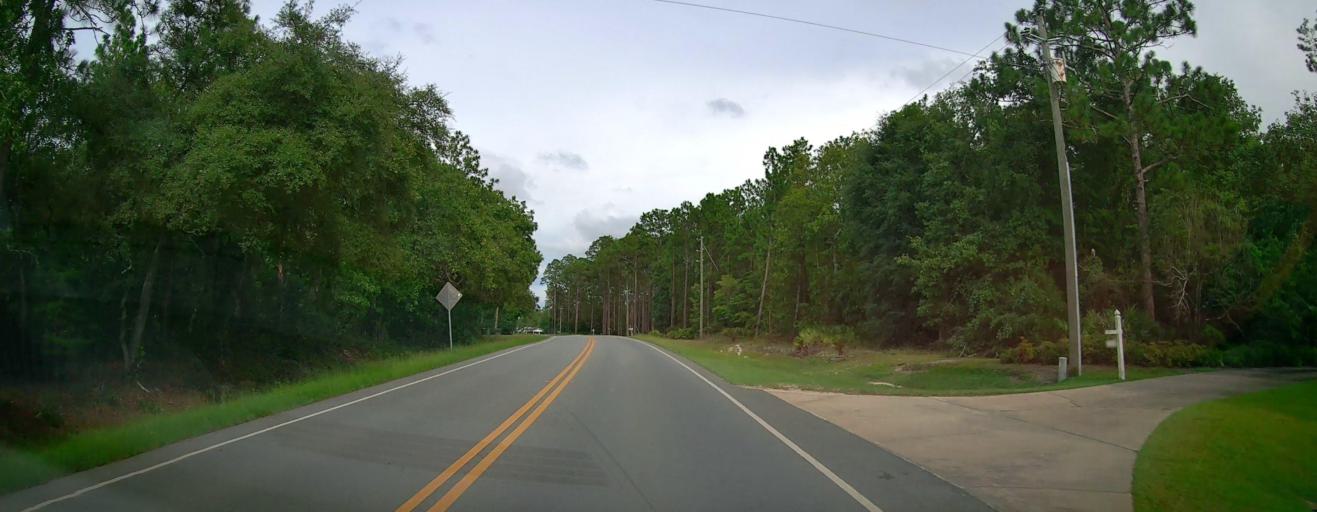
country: US
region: Georgia
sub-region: Wayne County
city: Jesup
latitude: 31.6573
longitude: -81.9075
